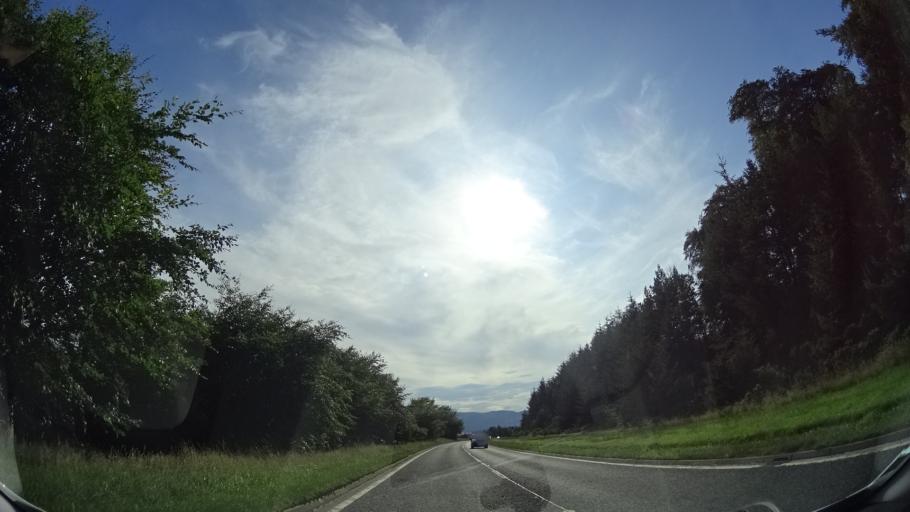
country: GB
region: Scotland
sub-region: Highland
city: Muir of Ord
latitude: 57.5591
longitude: -4.5003
